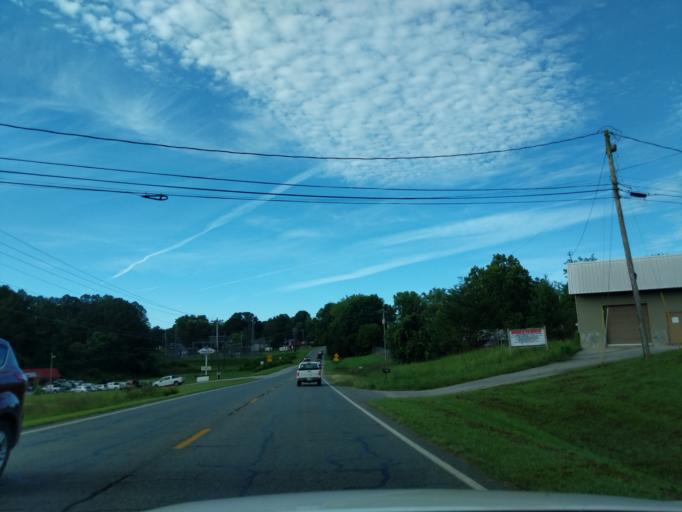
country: US
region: Georgia
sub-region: Fannin County
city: McCaysville
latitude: 34.9512
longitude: -84.3694
